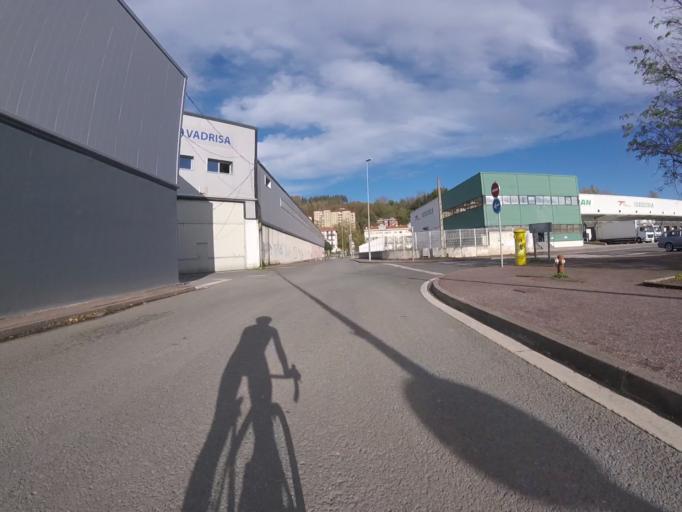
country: ES
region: Basque Country
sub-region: Provincia de Guipuzcoa
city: Hernani
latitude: 43.2709
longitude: -1.9642
